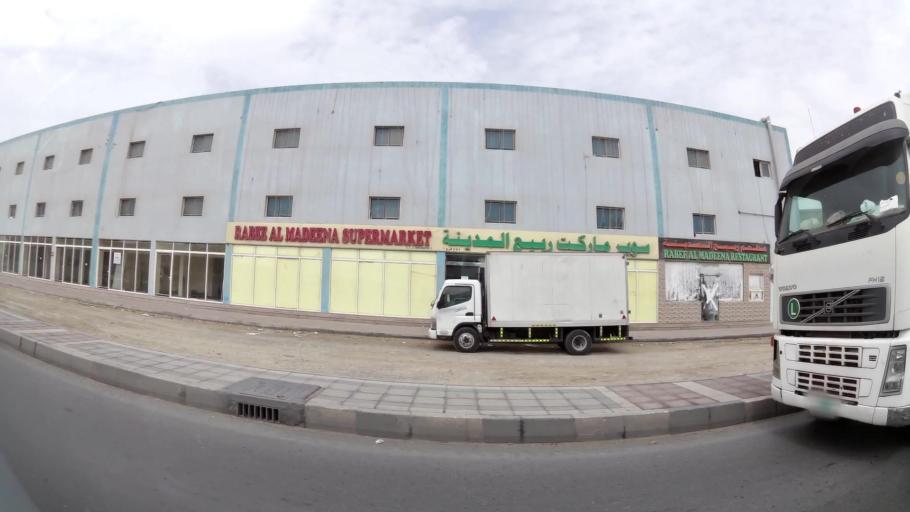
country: AE
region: Abu Dhabi
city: Abu Dhabi
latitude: 24.3543
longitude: 54.4865
